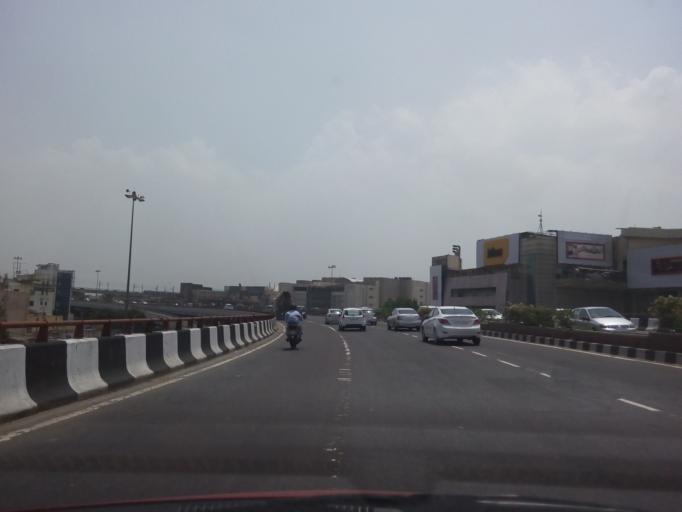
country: IN
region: NCT
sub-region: North West Delhi
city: Pitampura
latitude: 28.6540
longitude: 77.1246
